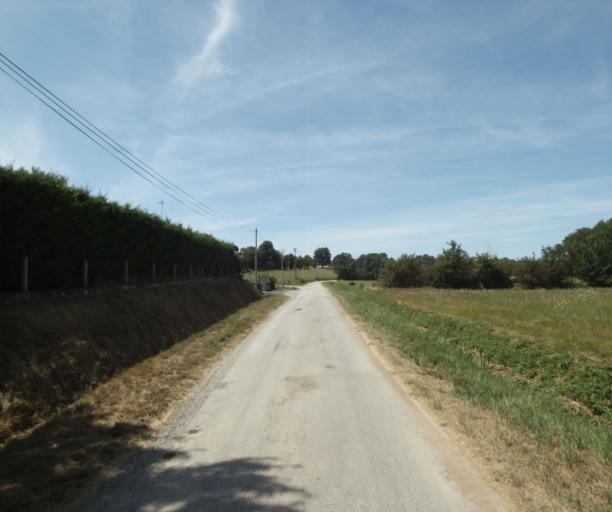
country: FR
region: Midi-Pyrenees
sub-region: Departement de la Haute-Garonne
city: Revel
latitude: 43.4926
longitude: 2.0200
